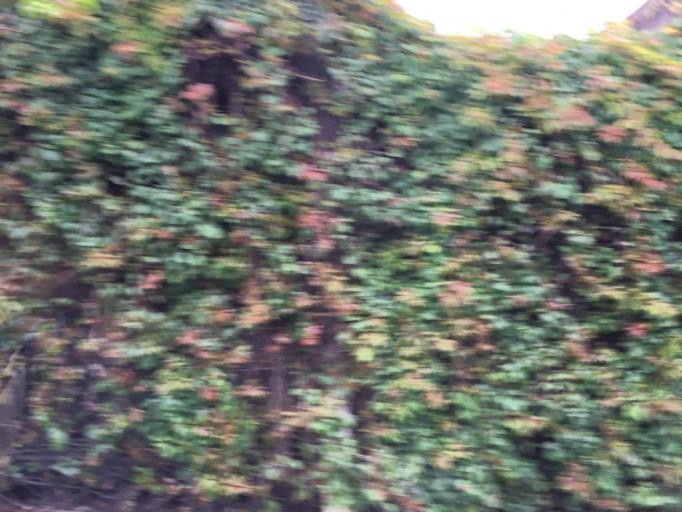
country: GT
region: Sacatepequez
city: Jocotenango
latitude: 14.5841
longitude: -90.7469
